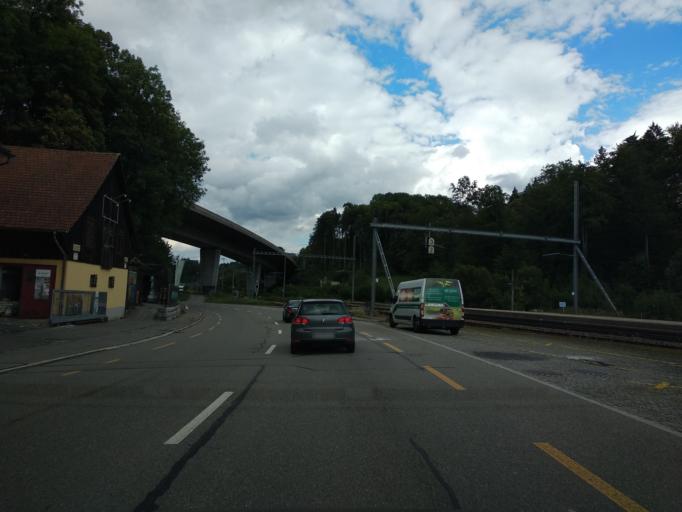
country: CH
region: Zurich
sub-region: Bezirk Winterthur
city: Toss
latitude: 47.4535
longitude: 8.7057
